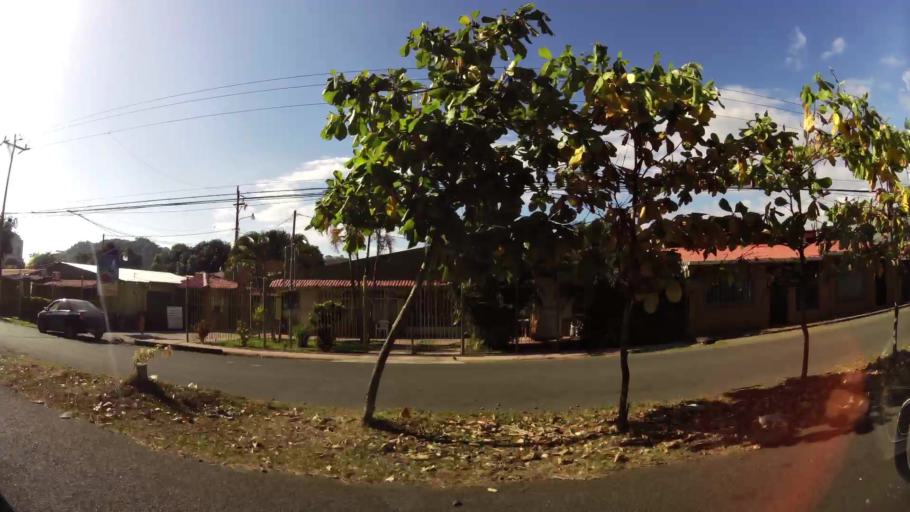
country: CR
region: Puntarenas
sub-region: Canton de Garabito
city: Jaco
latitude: 9.6245
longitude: -84.6355
